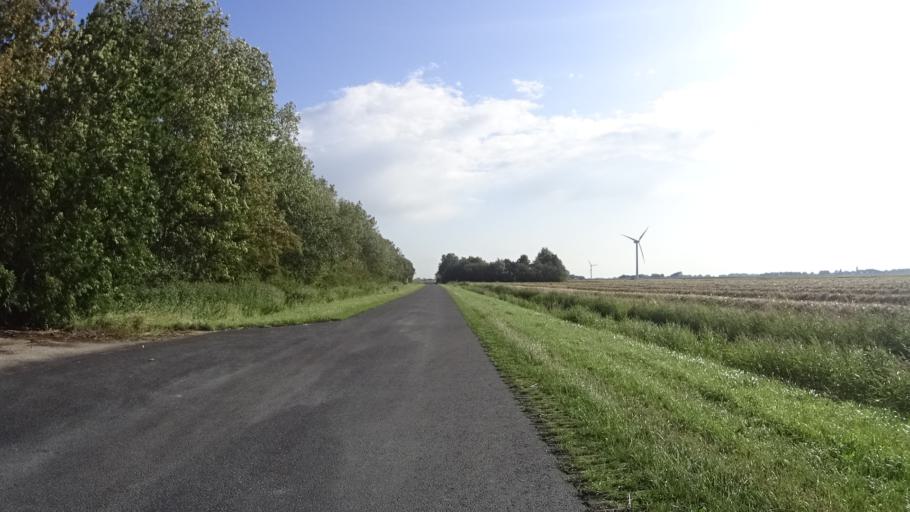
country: NL
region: Friesland
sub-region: Gemeente Harlingen
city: Harlingen
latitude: 53.1150
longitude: 5.4127
